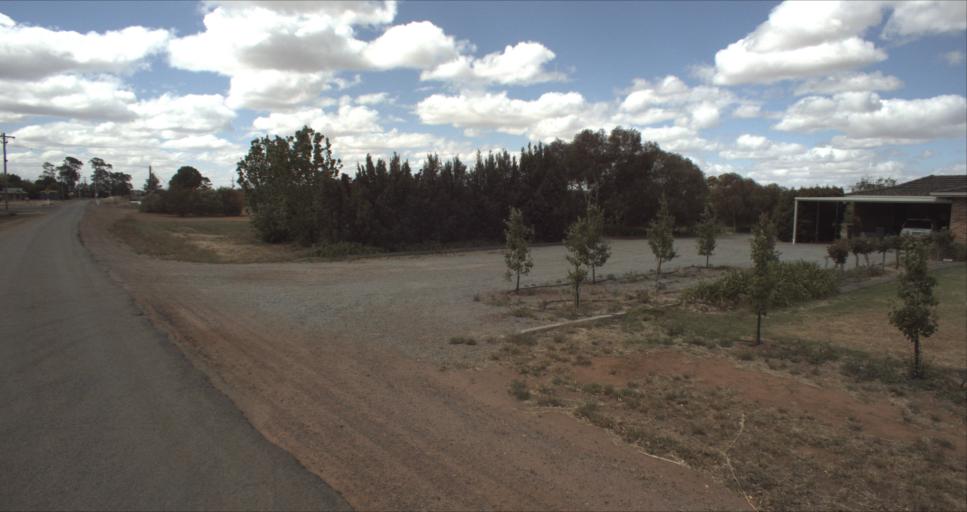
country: AU
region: New South Wales
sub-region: Leeton
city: Leeton
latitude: -34.5817
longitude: 146.3968
